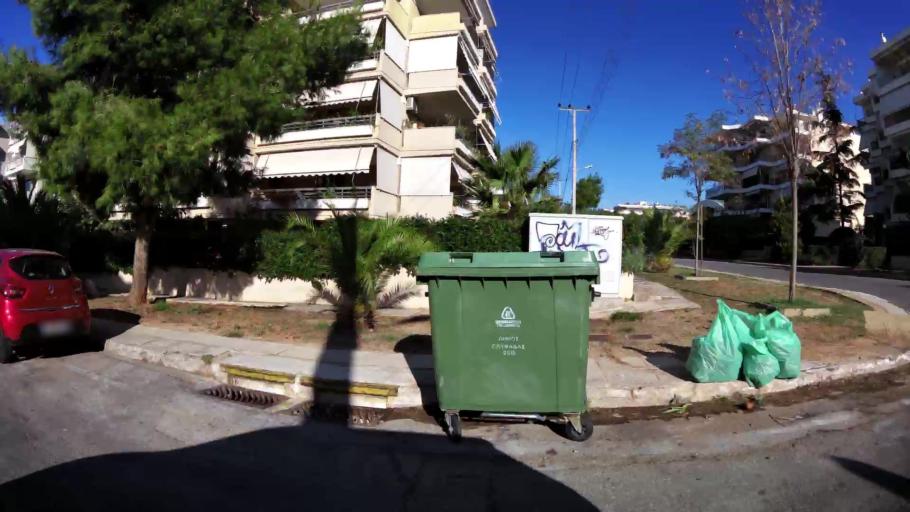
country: GR
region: Attica
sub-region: Nomarchia Athinas
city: Glyfada
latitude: 37.8688
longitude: 23.7619
